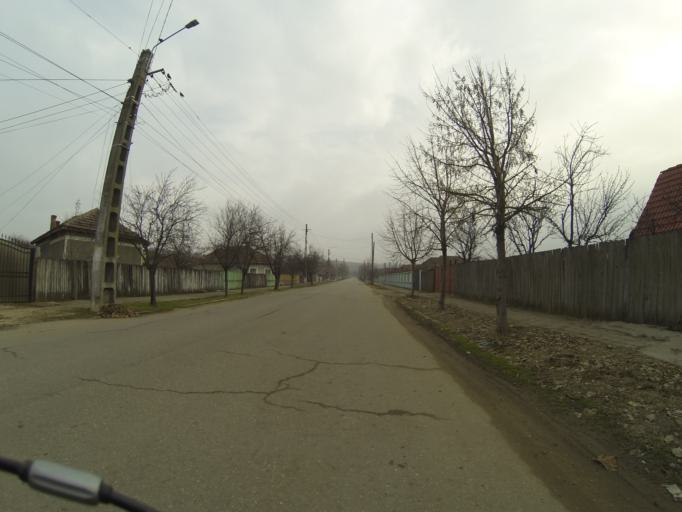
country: RO
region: Mehedinti
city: Vanju-Mare
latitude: 44.4217
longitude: 22.8726
